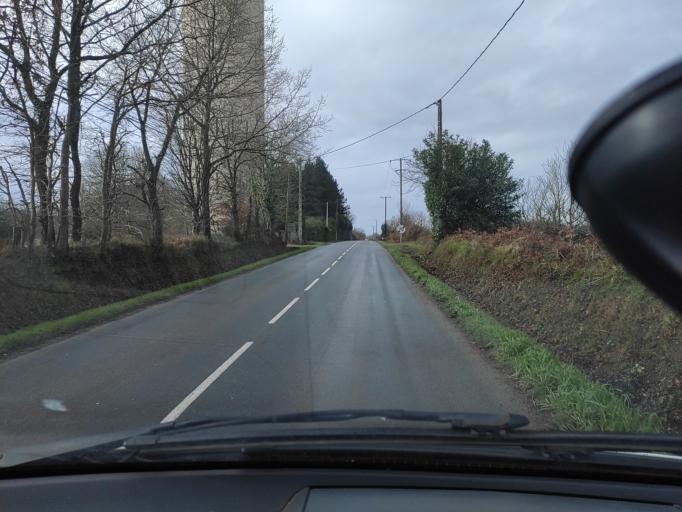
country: FR
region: Pays de la Loire
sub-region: Departement de la Vendee
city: La Boissiere-des-Landes
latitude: 46.5658
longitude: -1.4688
